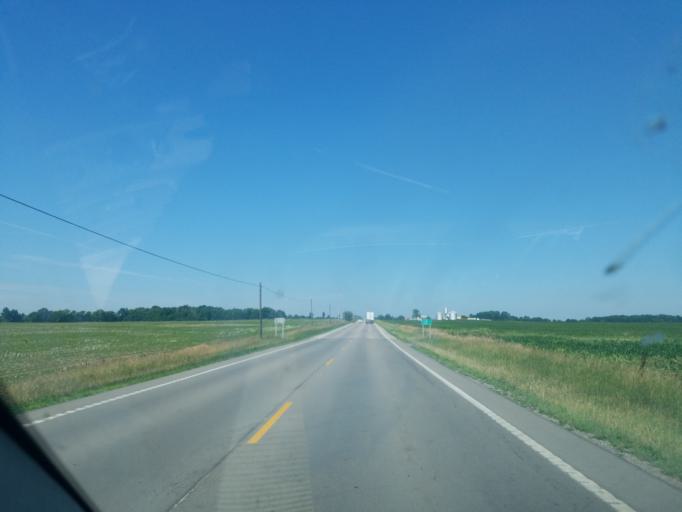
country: US
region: Ohio
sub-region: Shelby County
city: Jackson Center
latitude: 40.4393
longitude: -84.0016
